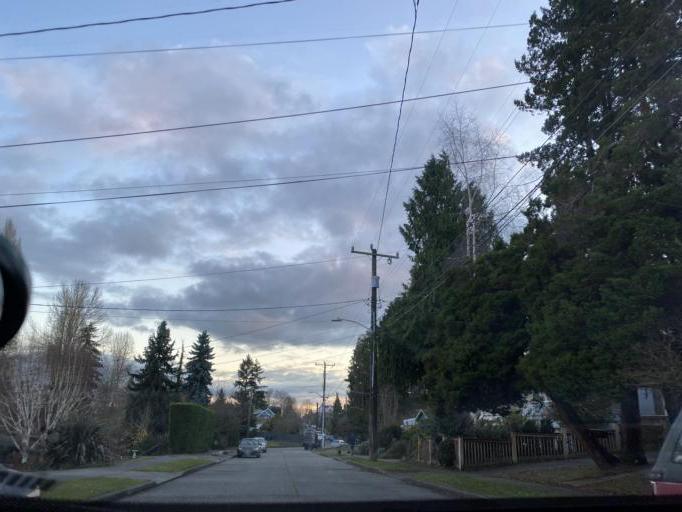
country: US
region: Washington
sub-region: King County
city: Seattle
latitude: 47.6476
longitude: -122.3874
